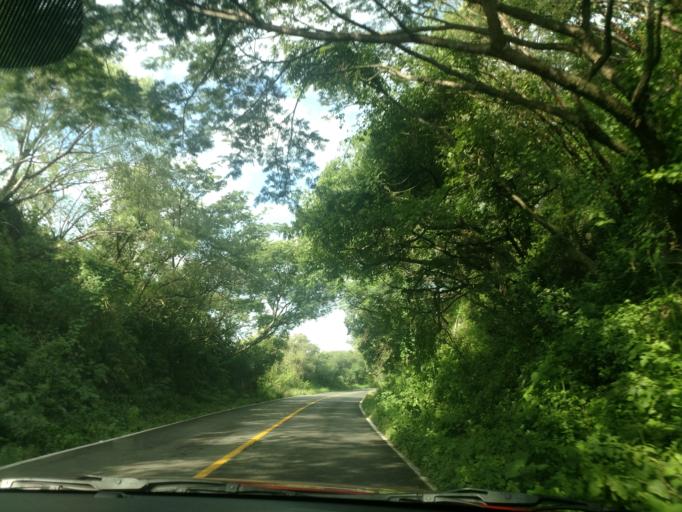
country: MX
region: Jalisco
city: Ameca
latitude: 20.5350
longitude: -104.1856
